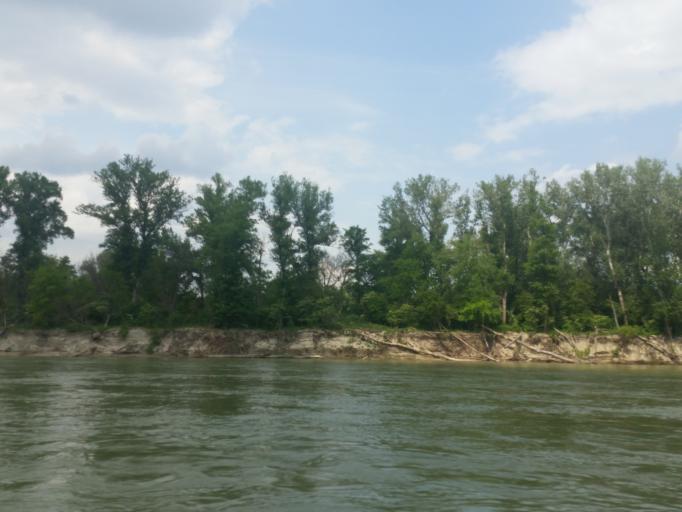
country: AT
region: Lower Austria
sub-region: Politischer Bezirk Bruck an der Leitha
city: Hainburg an der Donau
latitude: 48.1482
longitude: 16.9239
